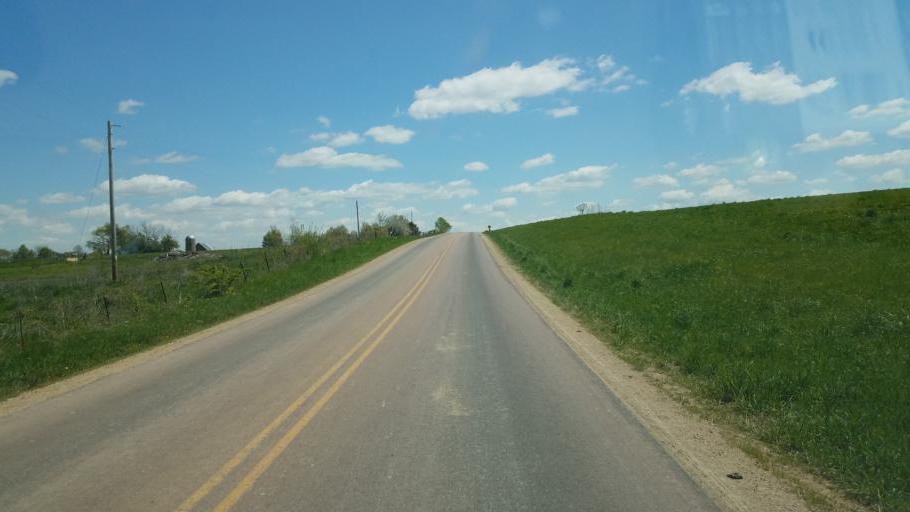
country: US
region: Wisconsin
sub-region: Vernon County
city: Hillsboro
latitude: 43.6462
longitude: -90.4499
